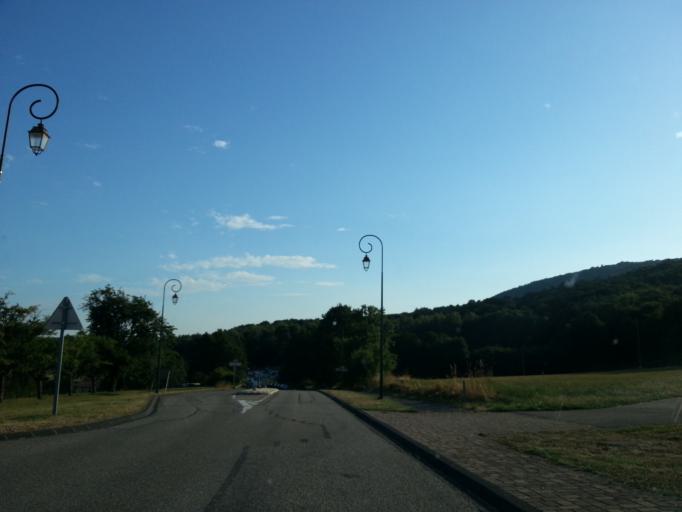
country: DE
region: Rheinland-Pfalz
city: Bobenthal
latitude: 49.0057
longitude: 7.8825
